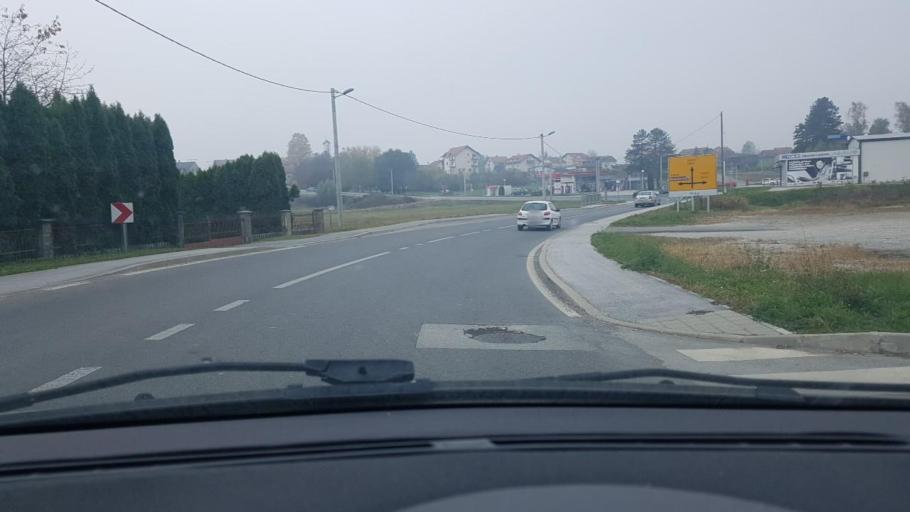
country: HR
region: Krapinsko-Zagorska
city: Zlatar
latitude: 46.0512
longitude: 16.0884
